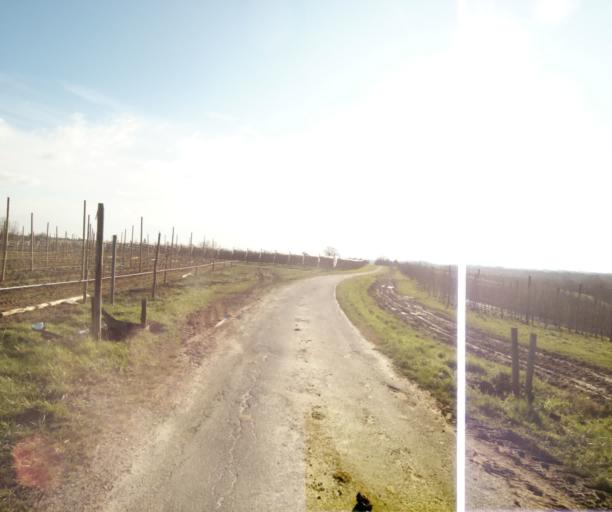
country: FR
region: Midi-Pyrenees
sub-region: Departement du Tarn-et-Garonne
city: Moissac
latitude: 44.1354
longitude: 1.0551
